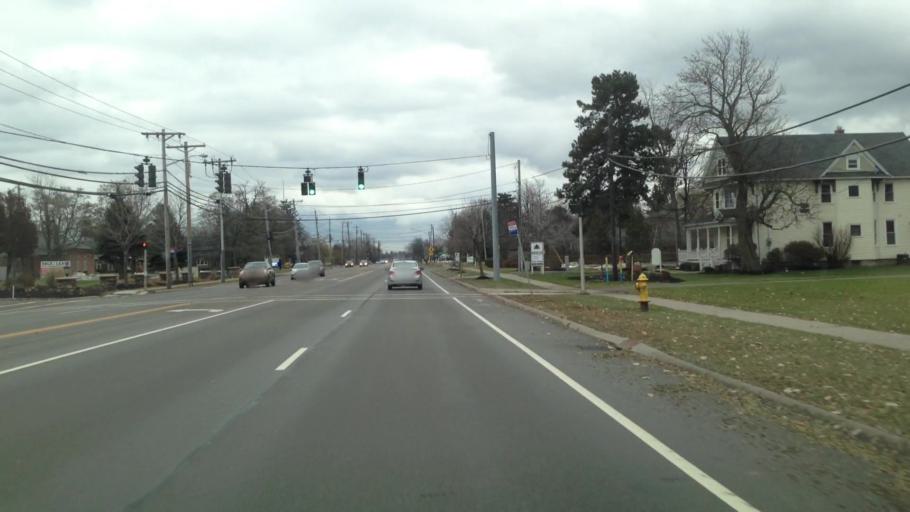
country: US
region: New York
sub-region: Erie County
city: Williamsville
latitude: 42.9659
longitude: -78.7137
